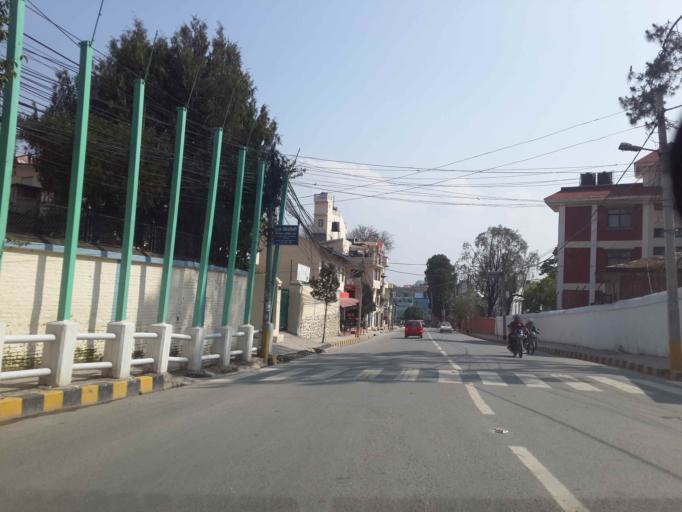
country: NP
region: Central Region
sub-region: Bagmati Zone
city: Kathmandu
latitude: 27.7262
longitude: 85.3306
